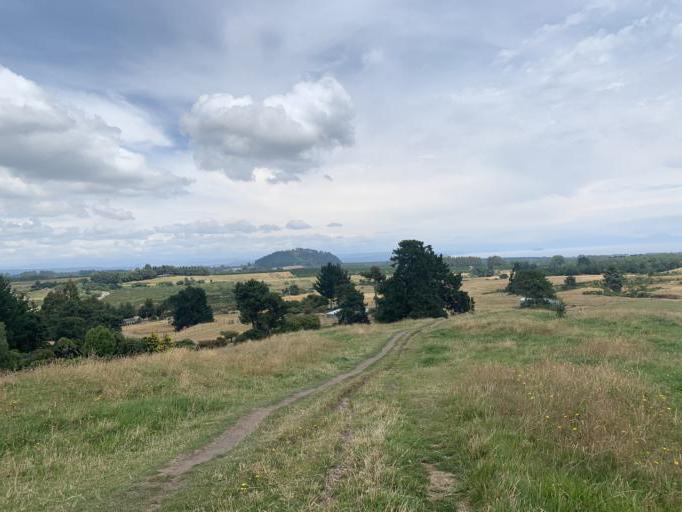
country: NZ
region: Waikato
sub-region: Taupo District
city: Taupo
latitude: -38.7027
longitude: 176.1417
